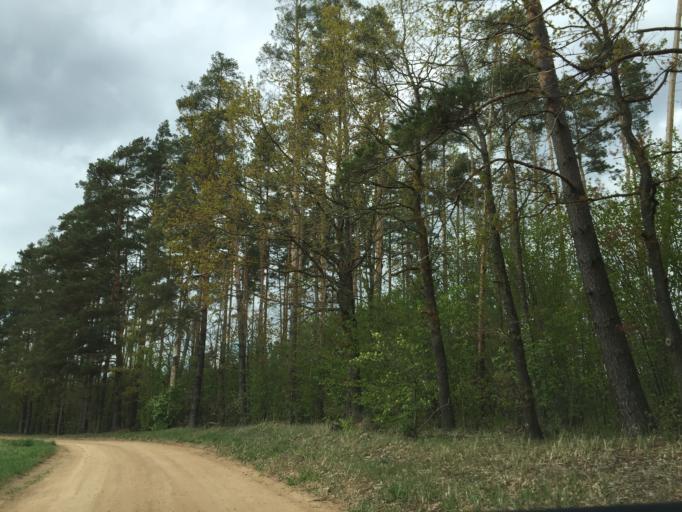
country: LV
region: Kekava
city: Kekava
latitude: 56.7996
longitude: 24.3060
